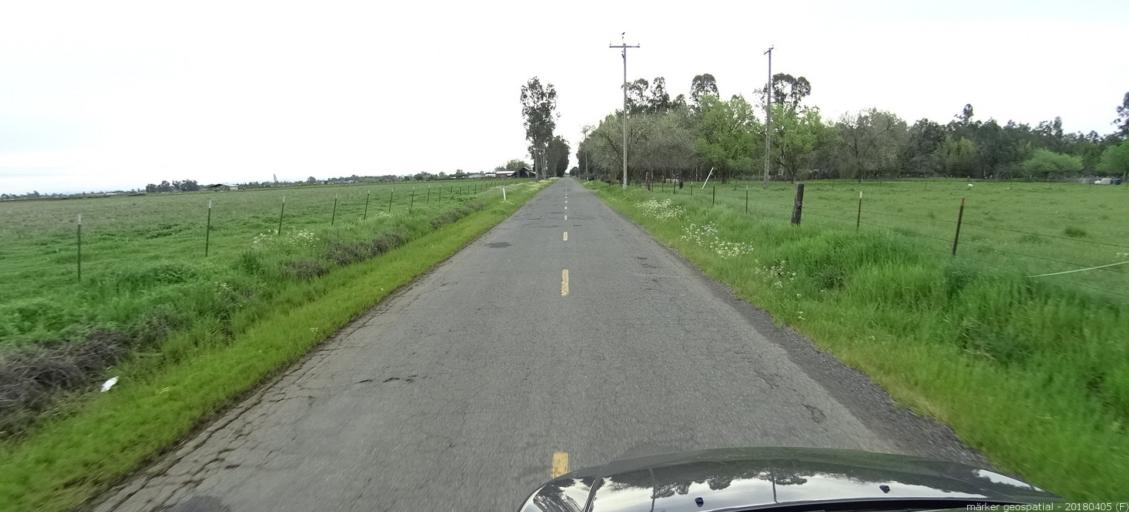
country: US
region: California
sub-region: Sacramento County
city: Herald
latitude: 38.2772
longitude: -121.2578
